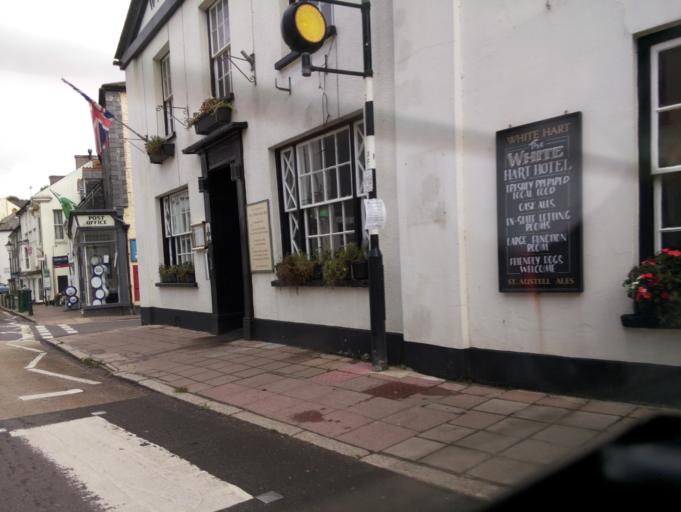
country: GB
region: England
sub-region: Devon
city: Modbury
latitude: 50.3492
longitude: -3.8871
